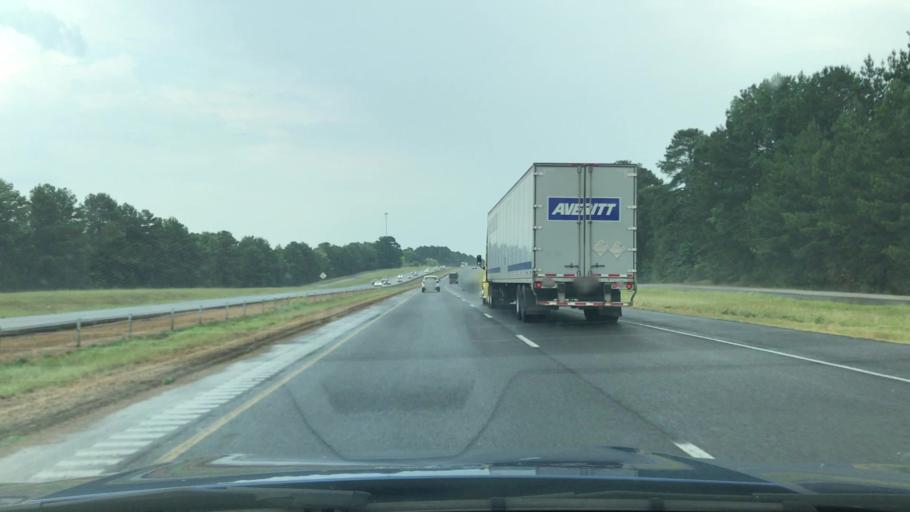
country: US
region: Texas
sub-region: Harrison County
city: Marshall
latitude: 32.4961
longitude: -94.2360
